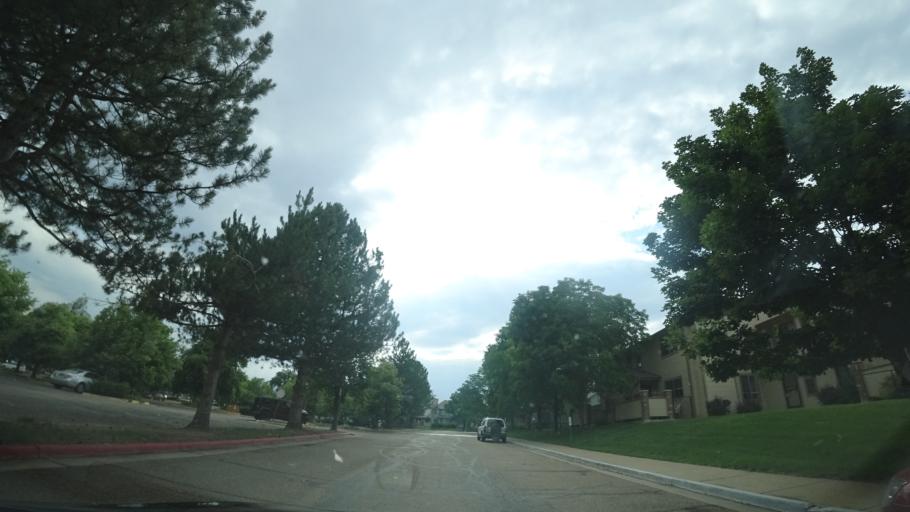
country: US
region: Colorado
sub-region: Jefferson County
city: Lakewood
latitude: 39.7133
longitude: -105.0980
